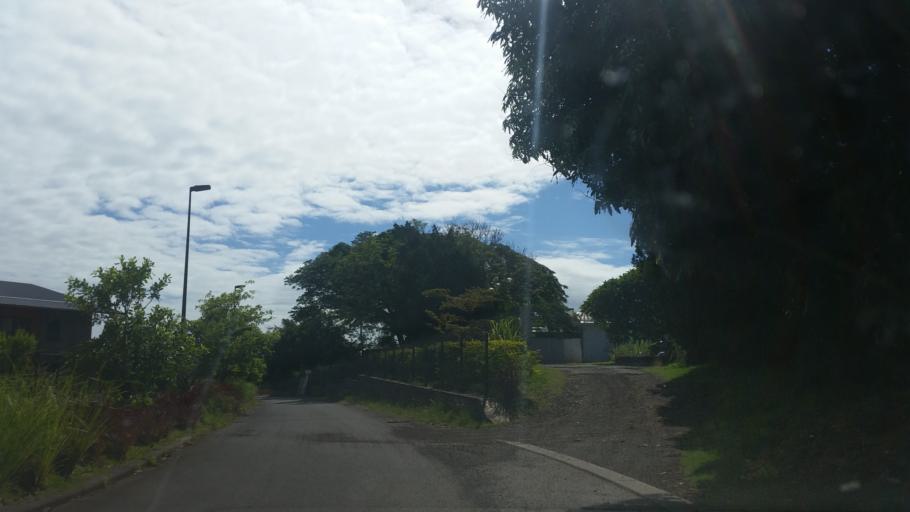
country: RE
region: Reunion
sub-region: Reunion
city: Sainte-Marie
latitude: -20.9084
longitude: 55.5003
